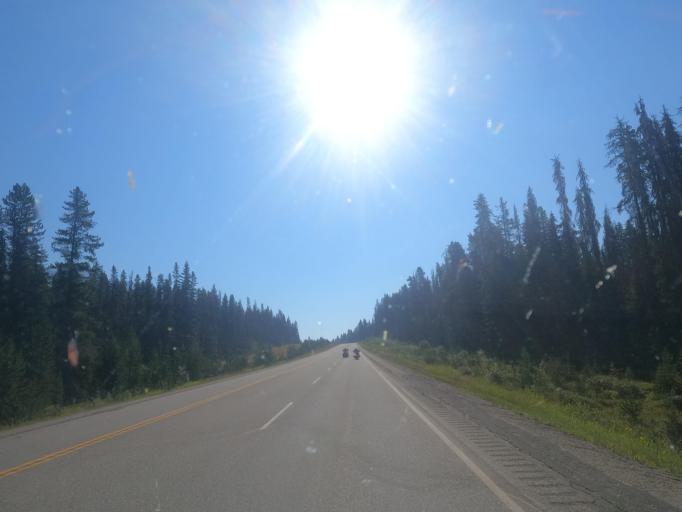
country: CA
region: Alberta
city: Grande Cache
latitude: 53.0059
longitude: -119.0550
